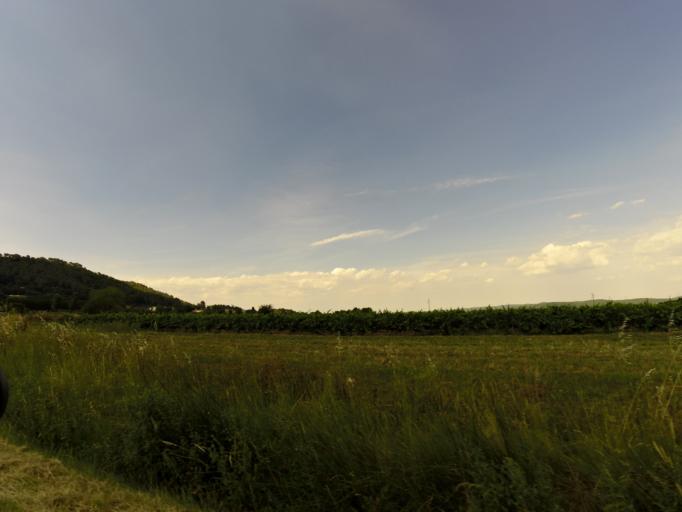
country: FR
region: Languedoc-Roussillon
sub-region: Departement du Gard
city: Sommieres
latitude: 43.8382
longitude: 4.0309
